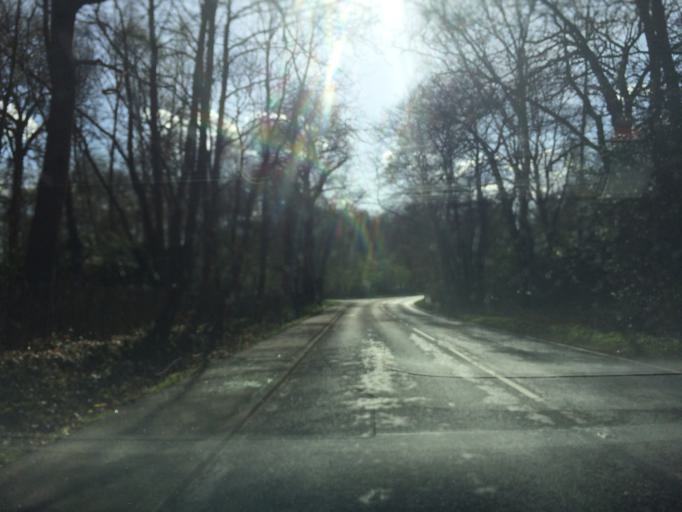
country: GB
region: England
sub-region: Surrey
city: Ottershaw
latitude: 51.3619
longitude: -0.5435
